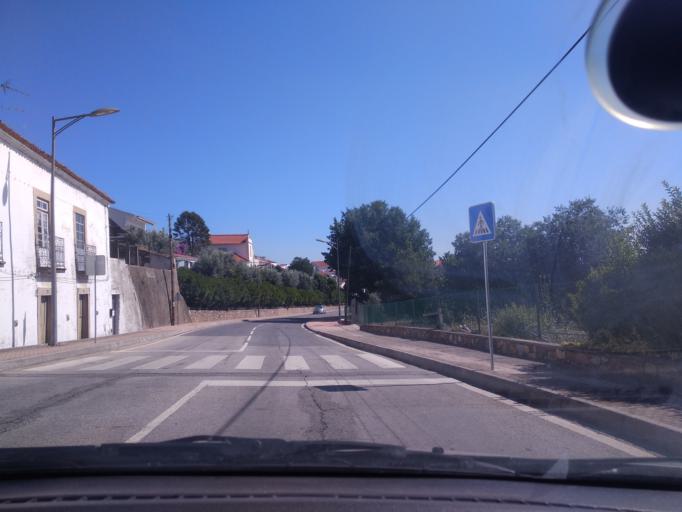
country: PT
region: Portalegre
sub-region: Nisa
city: Nisa
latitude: 39.6513
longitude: -7.6734
